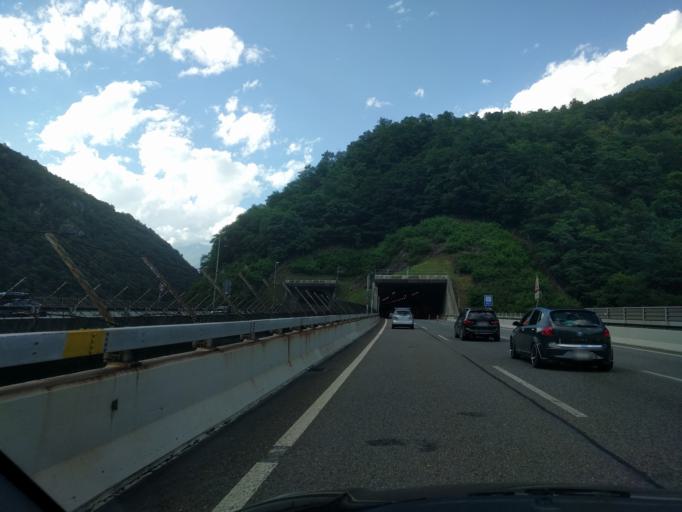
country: CH
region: Ticino
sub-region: Blenio District
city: Cancori
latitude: 46.4222
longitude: 8.8577
